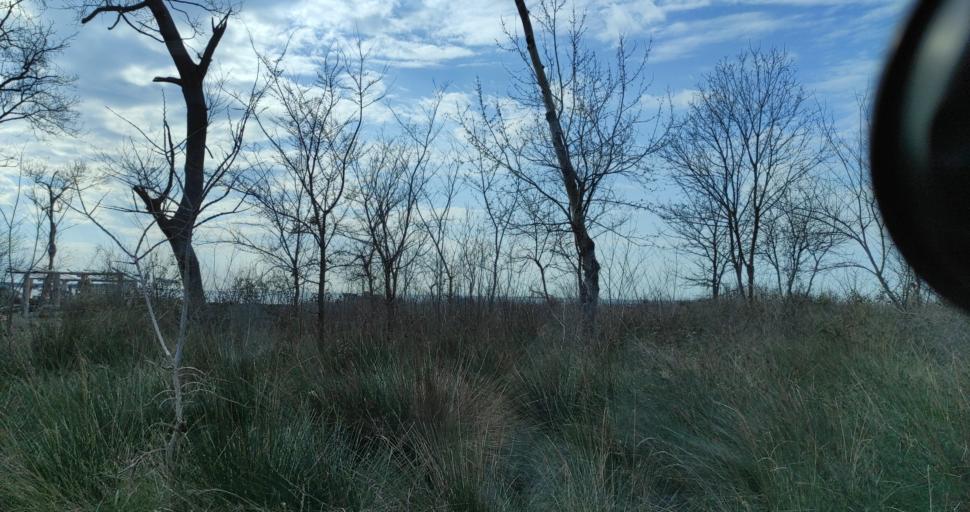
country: AL
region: Lezhe
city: Shengjin
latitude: 41.7763
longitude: 19.6032
